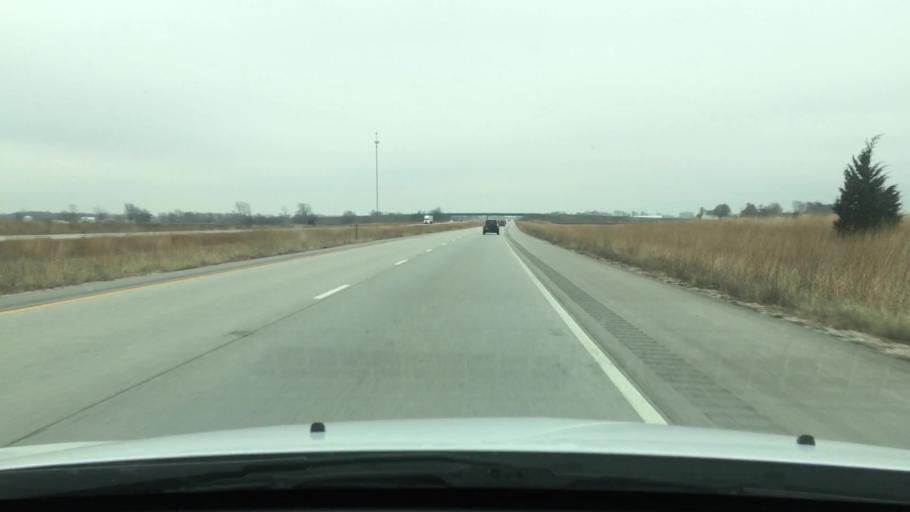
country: US
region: Illinois
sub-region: Morgan County
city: Jacksonville
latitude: 39.7382
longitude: -90.0887
